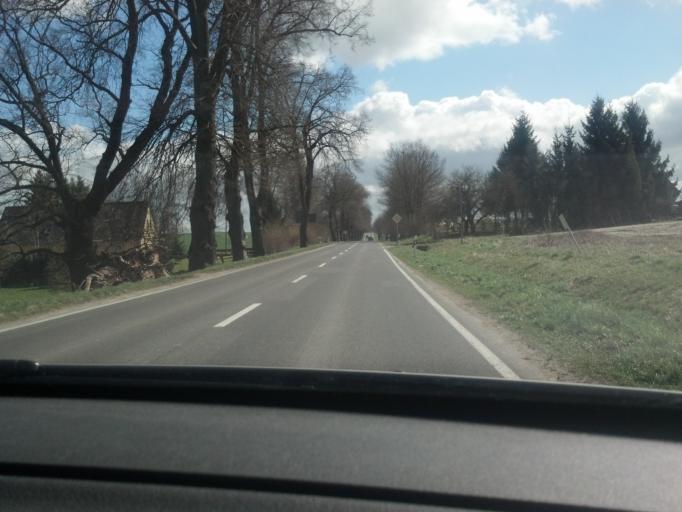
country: DE
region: Mecklenburg-Vorpommern
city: Loitz
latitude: 53.3878
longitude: 13.3407
